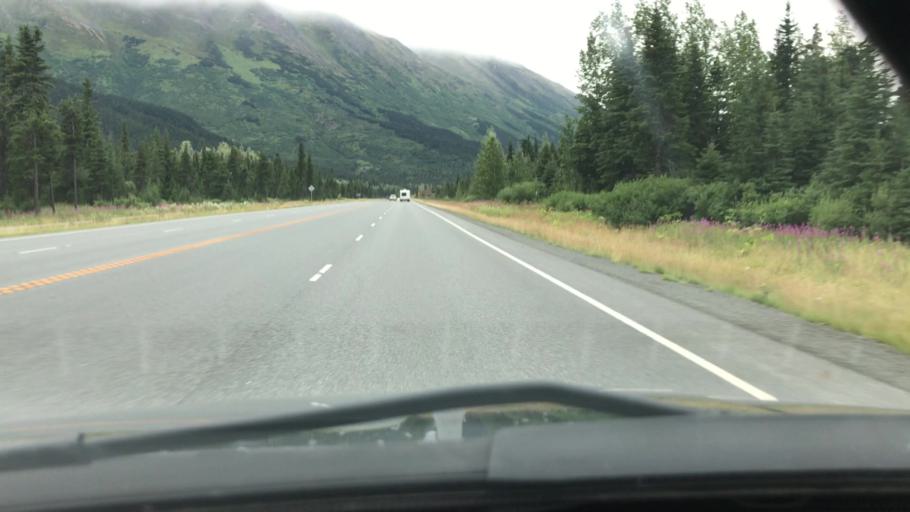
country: US
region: Alaska
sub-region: Anchorage Municipality
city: Girdwood
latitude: 60.7284
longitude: -149.3117
